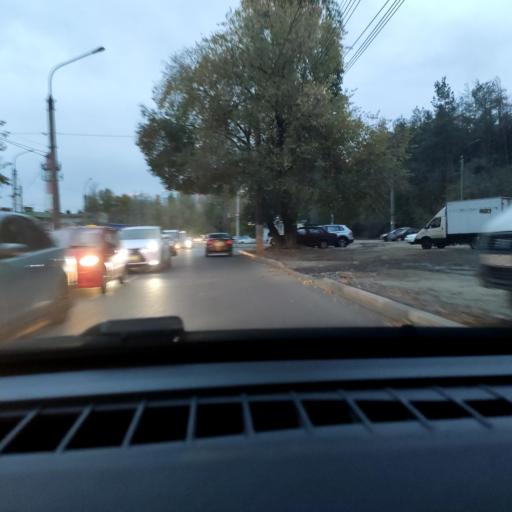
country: RU
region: Voronezj
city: Podgornoye
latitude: 51.6923
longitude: 39.1350
